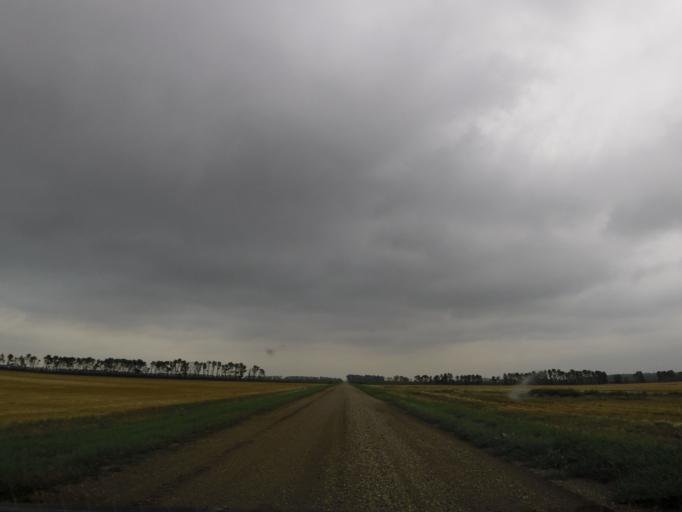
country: US
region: North Dakota
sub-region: Walsh County
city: Grafton
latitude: 48.4890
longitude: -97.1689
